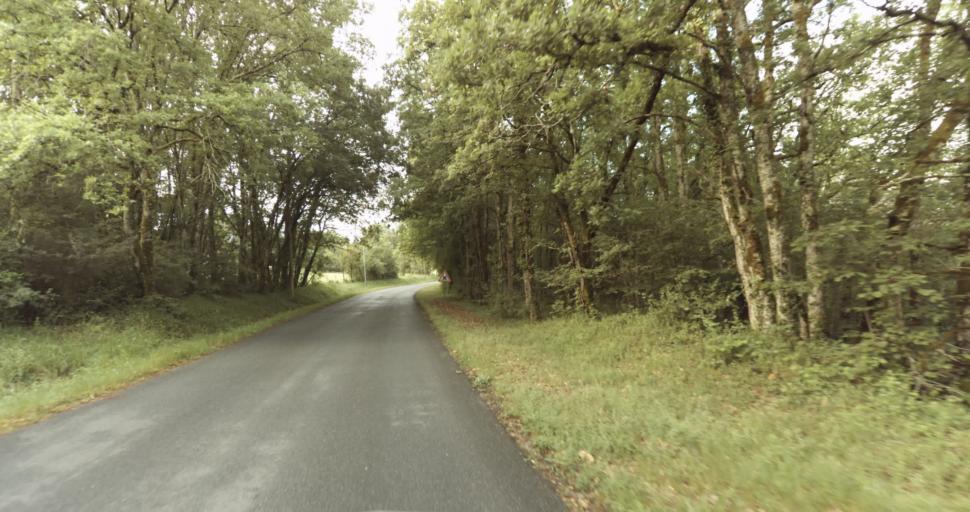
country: FR
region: Aquitaine
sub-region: Departement de la Dordogne
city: Lalinde
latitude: 44.9131
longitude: 0.7939
